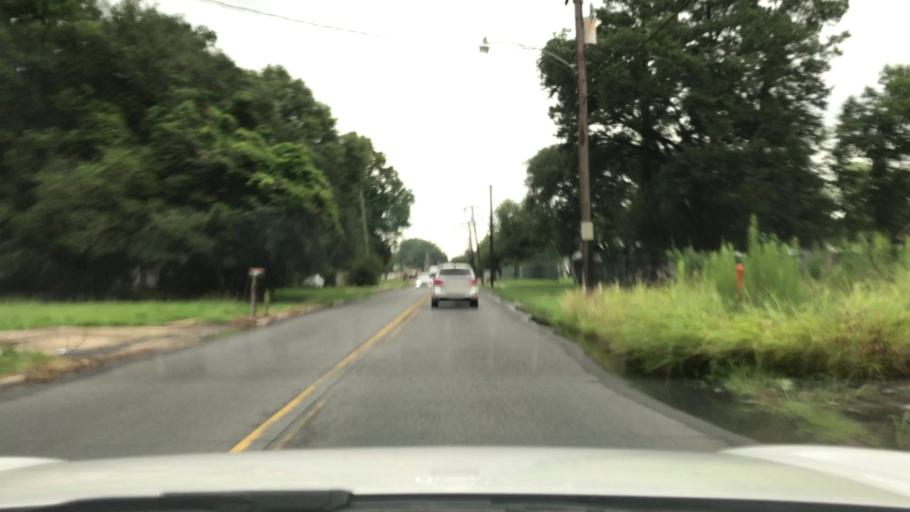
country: US
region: Louisiana
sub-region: East Baton Rouge Parish
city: Merrydale
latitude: 30.4763
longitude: -91.1174
